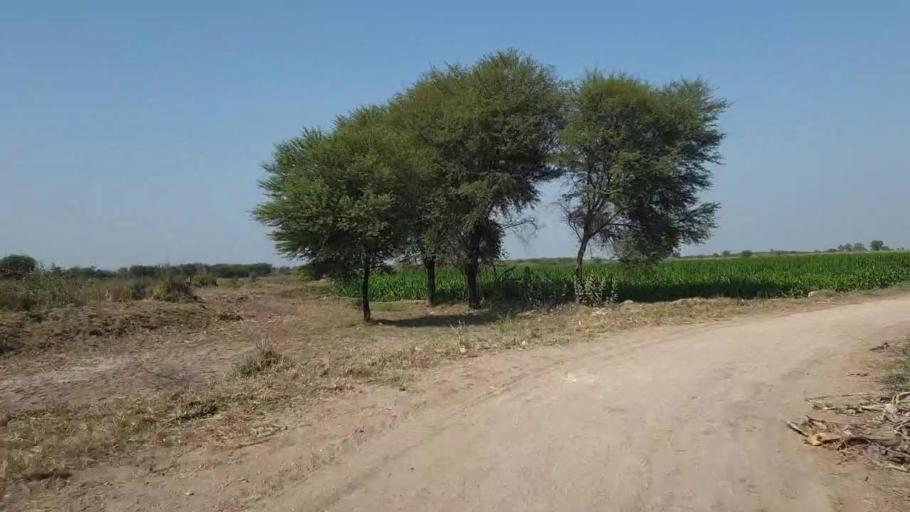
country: PK
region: Sindh
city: Hala
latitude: 25.9646
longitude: 68.4333
